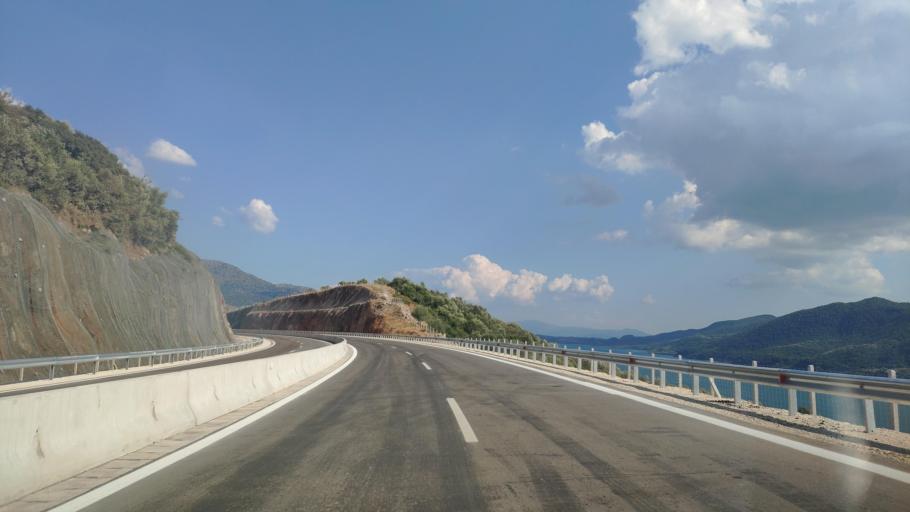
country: GR
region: West Greece
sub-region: Nomos Aitolias kai Akarnanias
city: Stanos
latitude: 38.7731
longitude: 21.1576
